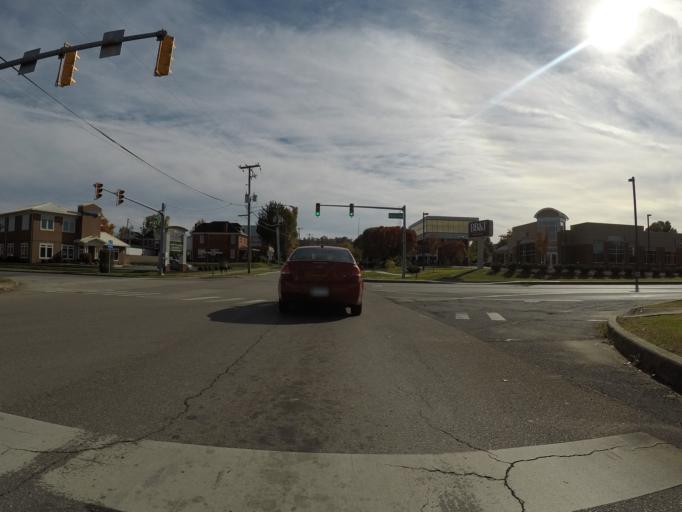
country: US
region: West Virginia
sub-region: Cabell County
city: Huntington
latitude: 38.4173
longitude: -82.4573
